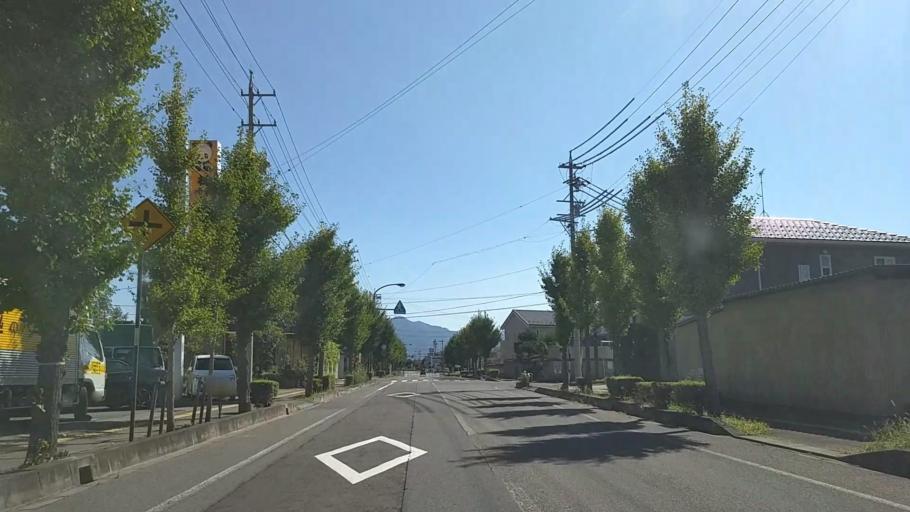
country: JP
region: Nagano
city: Nagano-shi
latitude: 36.5814
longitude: 138.1362
